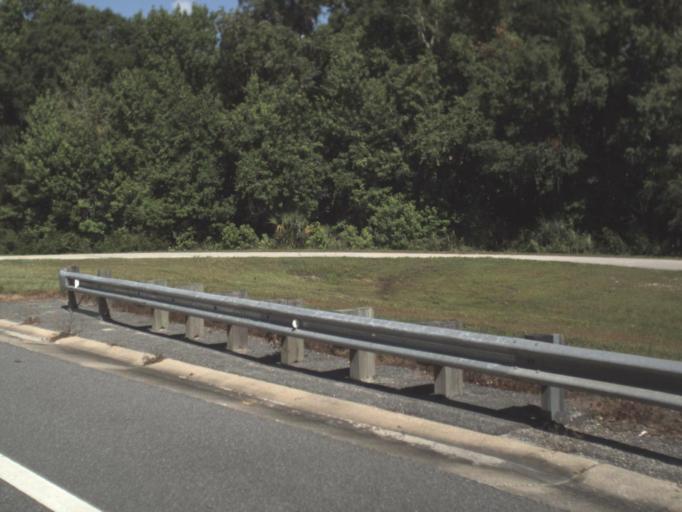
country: US
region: Florida
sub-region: Putnam County
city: Palatka
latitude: 29.5751
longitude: -81.6317
